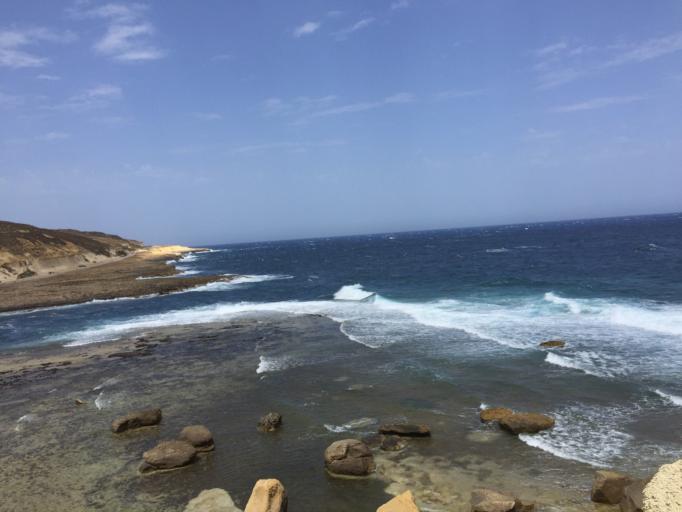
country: MT
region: Iz-Zebbug
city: Zebbug
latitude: 36.0796
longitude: 14.2496
